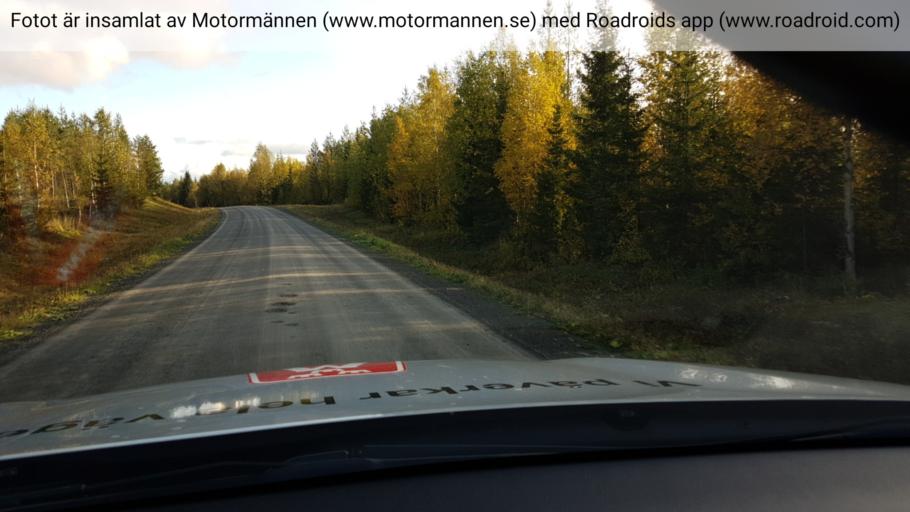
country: SE
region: Jaemtland
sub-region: Krokoms Kommun
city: Krokom
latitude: 63.7175
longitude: 14.5169
